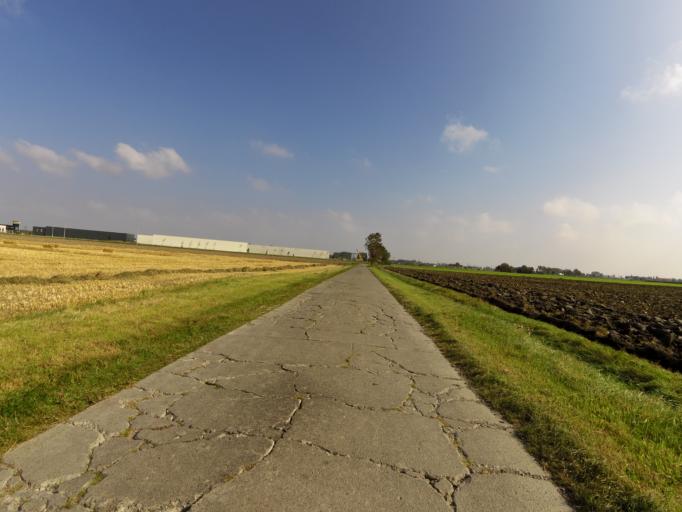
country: BE
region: Flanders
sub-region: Provincie West-Vlaanderen
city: Ostend
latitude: 51.1904
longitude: 2.8935
